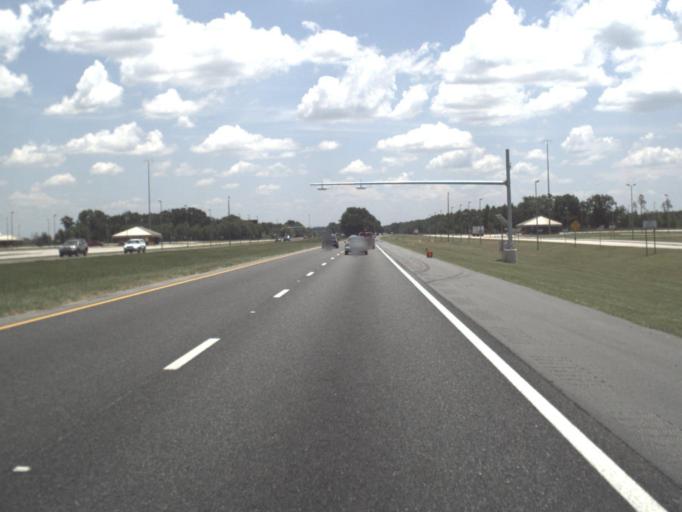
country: US
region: Florida
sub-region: Madison County
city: Madison
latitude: 30.3748
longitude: -83.2759
